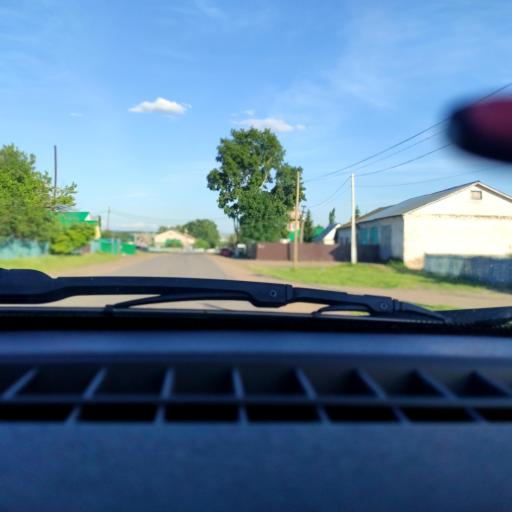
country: RU
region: Bashkortostan
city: Tolbazy
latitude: 54.2932
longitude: 55.8107
